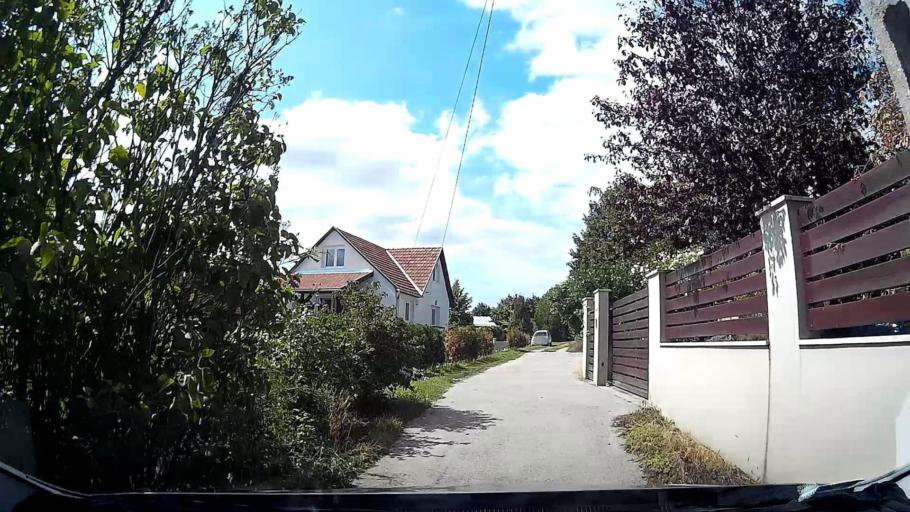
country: HU
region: Pest
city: Szentendre
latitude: 47.6879
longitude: 19.0655
